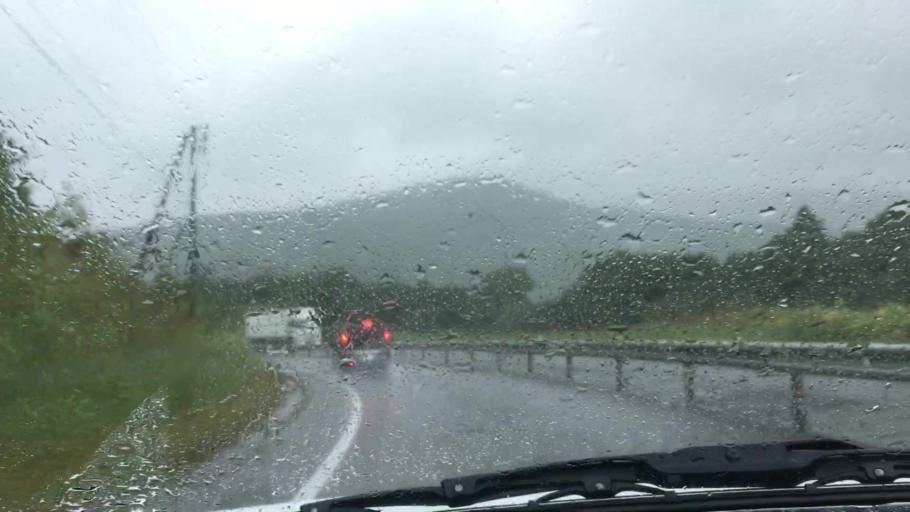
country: JP
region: Hokkaido
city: Sapporo
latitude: 42.8526
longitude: 141.0802
